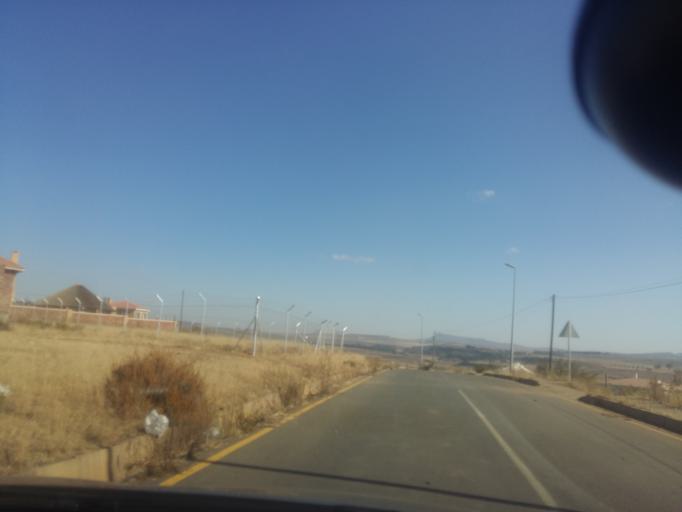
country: LS
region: Maseru
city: Maseru
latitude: -29.3426
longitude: 27.4467
